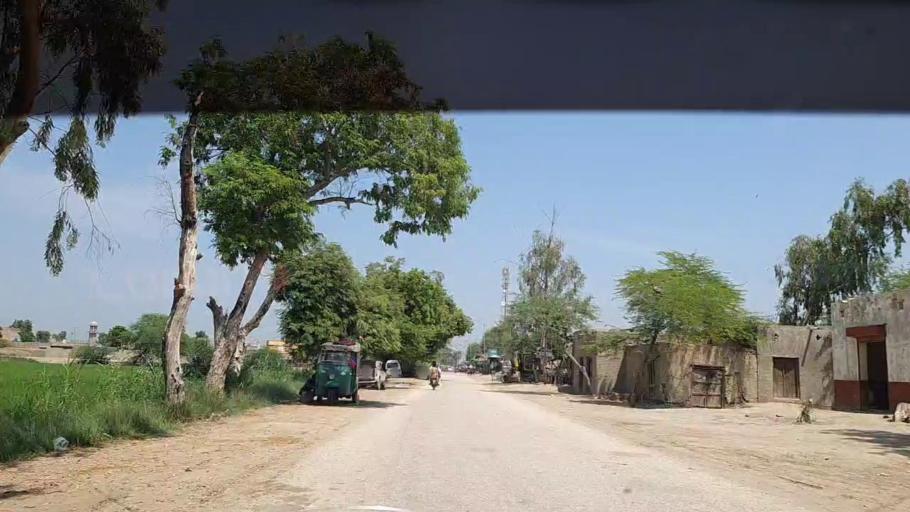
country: PK
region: Sindh
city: Rustam jo Goth
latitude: 28.0774
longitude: 68.7844
